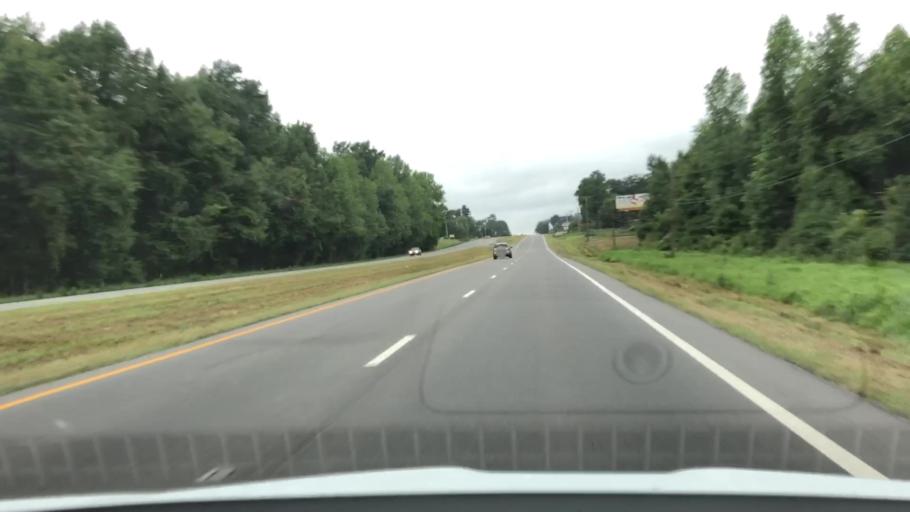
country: US
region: North Carolina
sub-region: Lenoir County
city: La Grange
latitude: 35.2742
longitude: -77.7441
